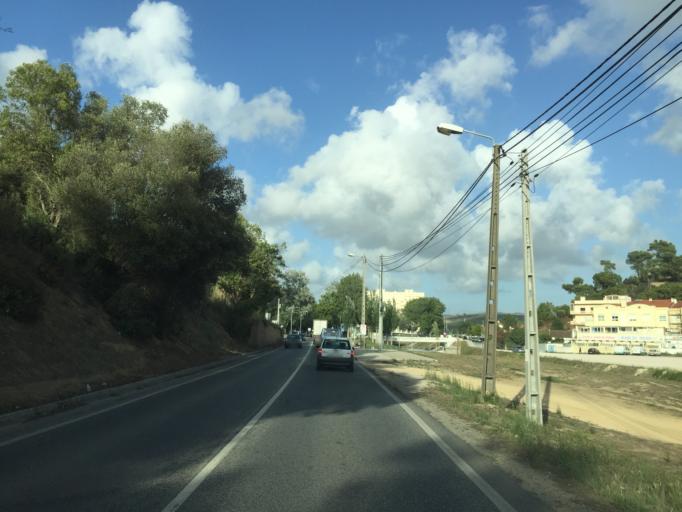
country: PT
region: Lisbon
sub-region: Torres Vedras
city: Torres Vedras
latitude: 39.0960
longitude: -9.2645
